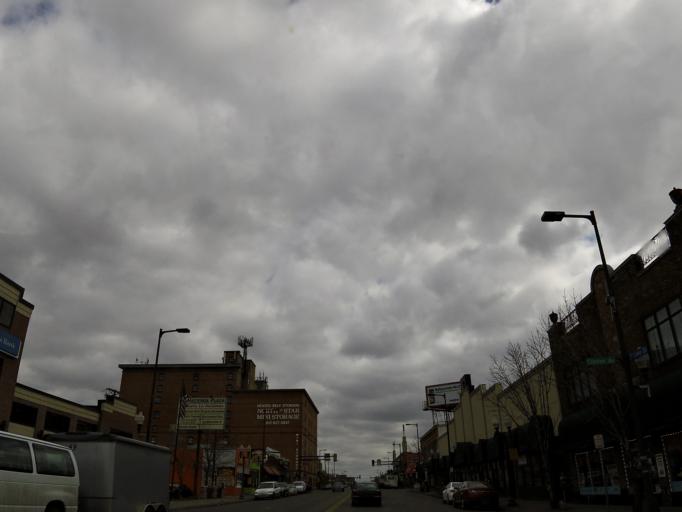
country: US
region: Minnesota
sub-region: Hennepin County
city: Minneapolis
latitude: 44.9483
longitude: -93.2717
